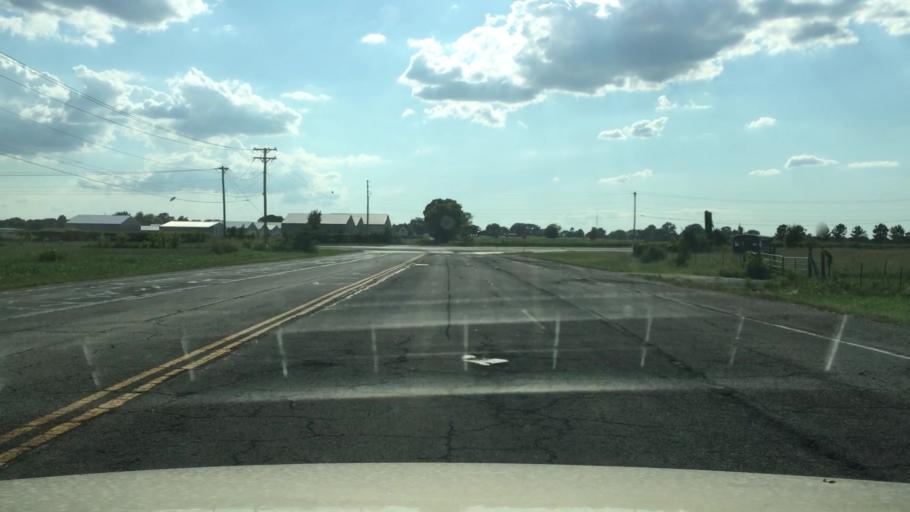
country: US
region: Oklahoma
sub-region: Cherokee County
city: Tahlequah
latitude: 35.9299
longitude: -94.9990
